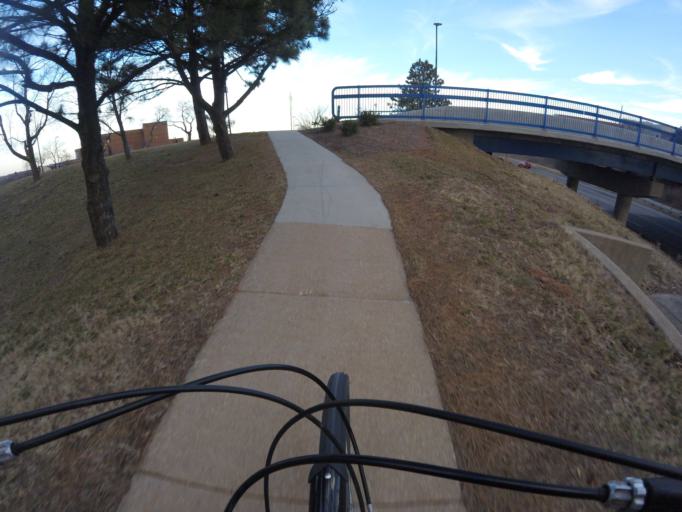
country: US
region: Kansas
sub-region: Douglas County
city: Lawrence
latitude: 38.9476
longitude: -95.2609
